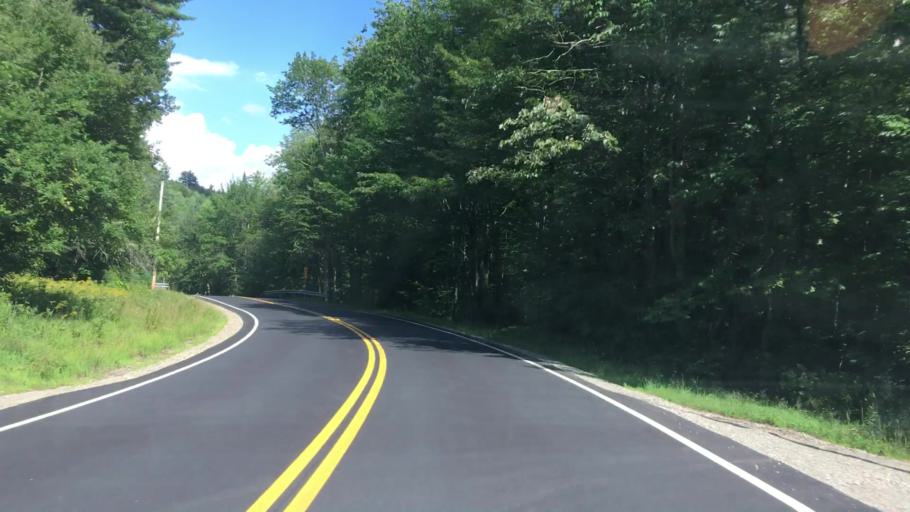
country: US
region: New Hampshire
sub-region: Grafton County
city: North Haverhill
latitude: 44.1054
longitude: -71.8715
